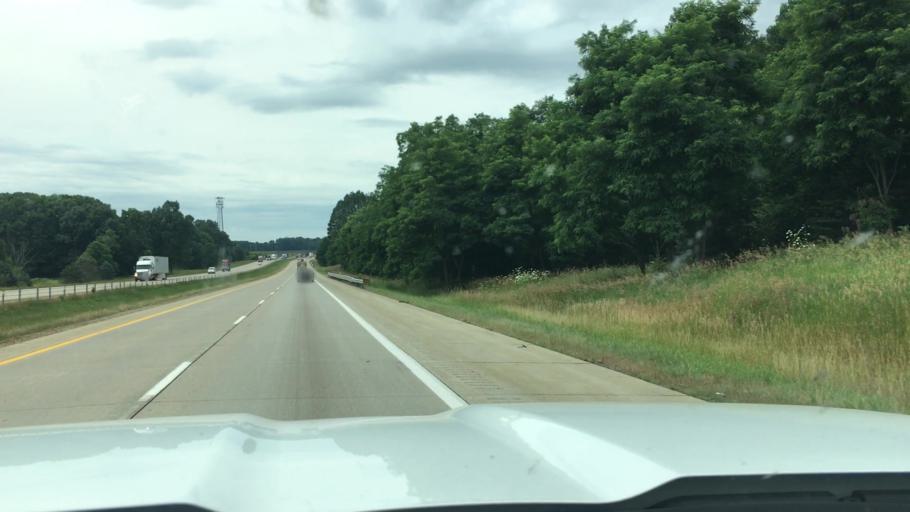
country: US
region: Michigan
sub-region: Allegan County
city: Otsego
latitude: 42.5016
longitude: -85.6533
